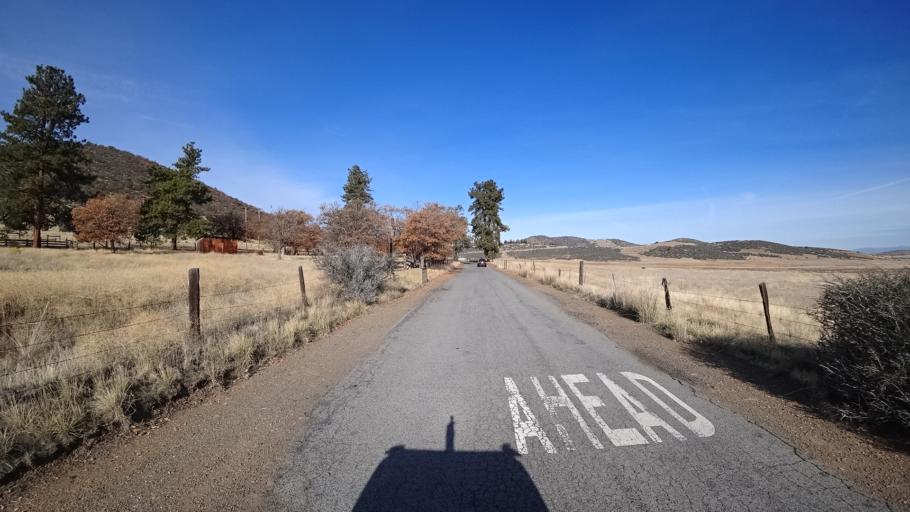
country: US
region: California
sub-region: Siskiyou County
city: Montague
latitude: 41.6387
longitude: -122.5736
